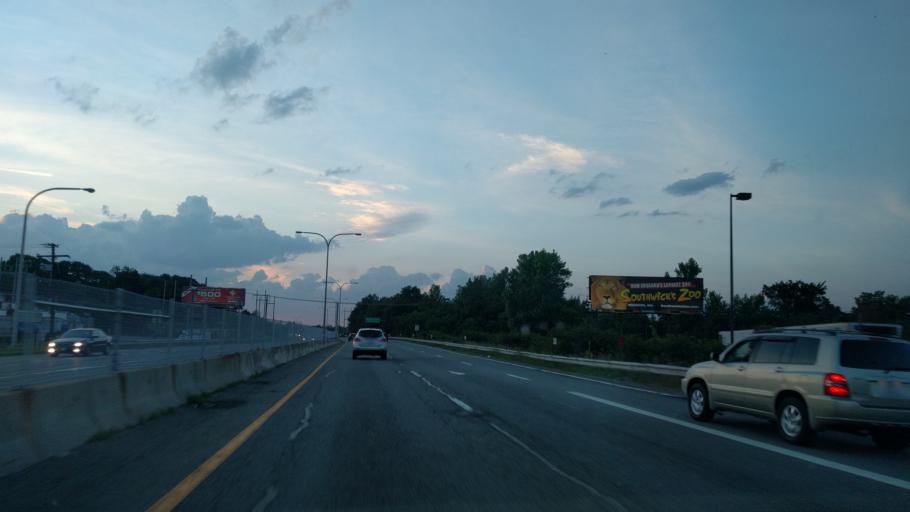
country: US
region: Rhode Island
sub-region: Providence County
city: Providence
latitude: 41.8429
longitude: -71.4191
